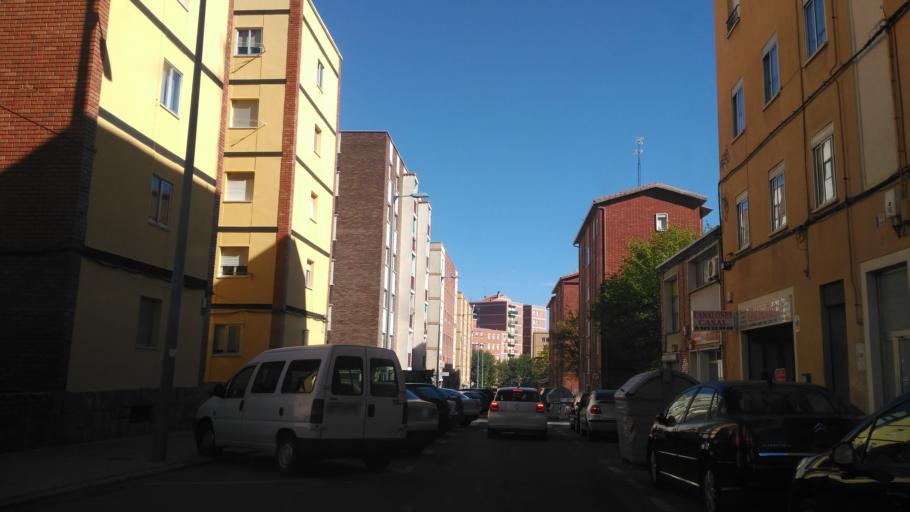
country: ES
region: Castille and Leon
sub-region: Provincia de Salamanca
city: Salamanca
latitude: 40.9752
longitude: -5.6526
